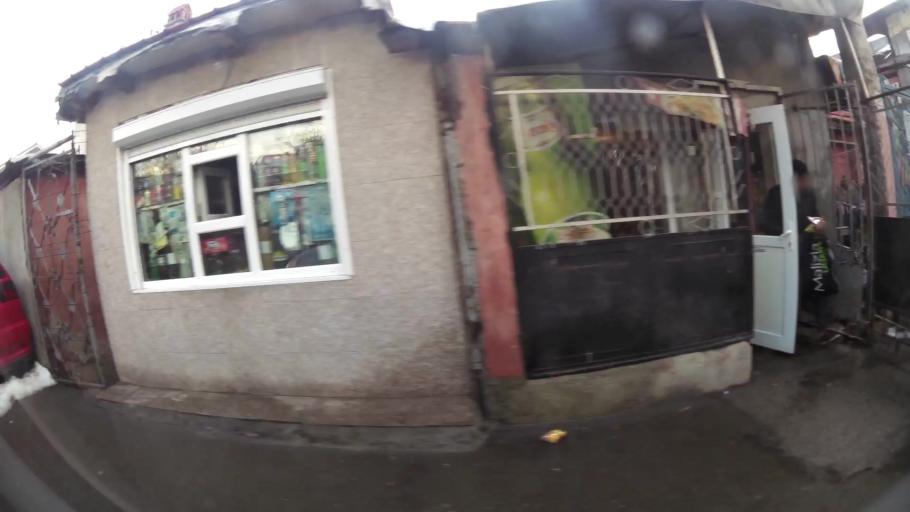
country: BG
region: Sofia-Capital
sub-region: Stolichna Obshtina
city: Sofia
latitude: 42.6943
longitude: 23.2691
